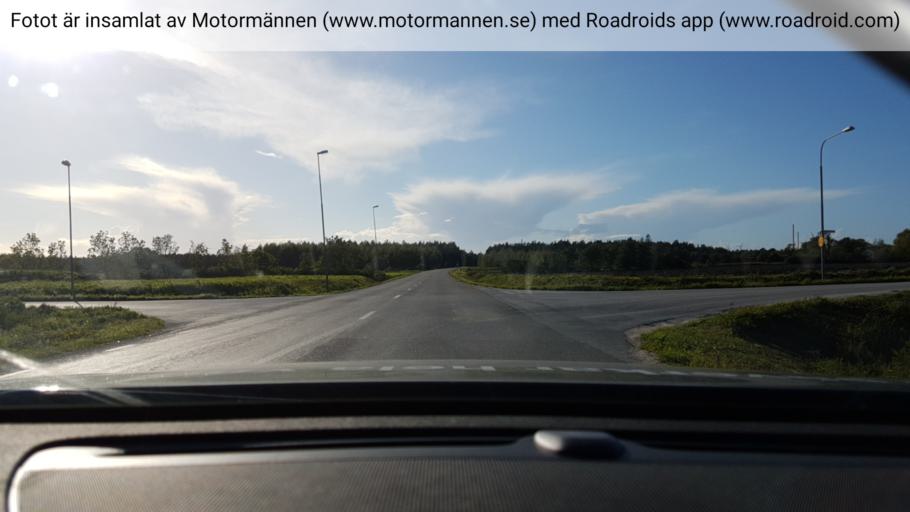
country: SE
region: Gotland
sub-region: Gotland
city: Klintehamn
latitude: 57.3803
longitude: 18.2221
